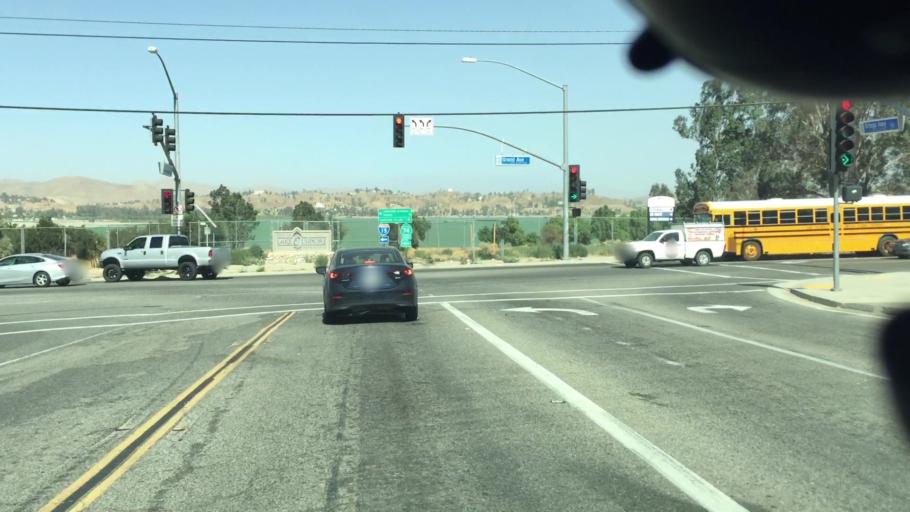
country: US
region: California
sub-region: Riverside County
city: Lakeland Village
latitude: 33.6580
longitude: -117.3760
